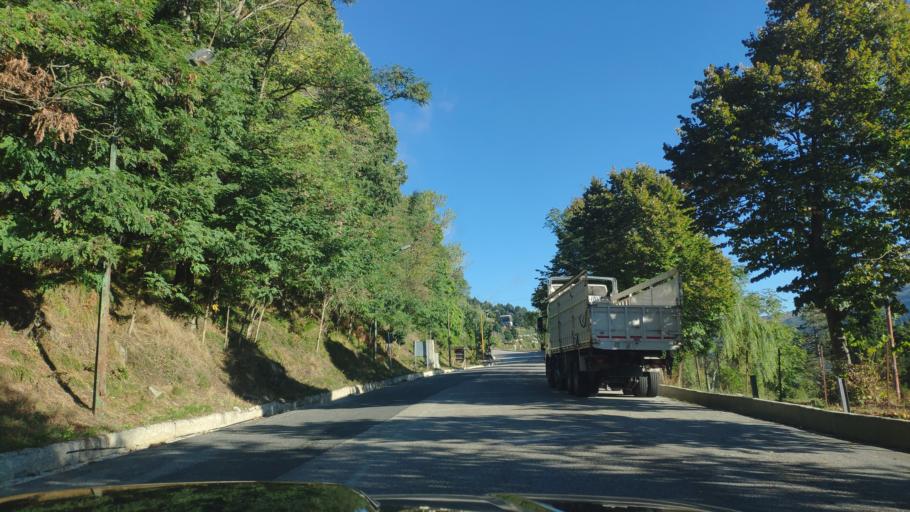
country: GR
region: Epirus
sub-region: Nomos Ioanninon
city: Metsovo
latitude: 39.7678
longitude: 21.1765
